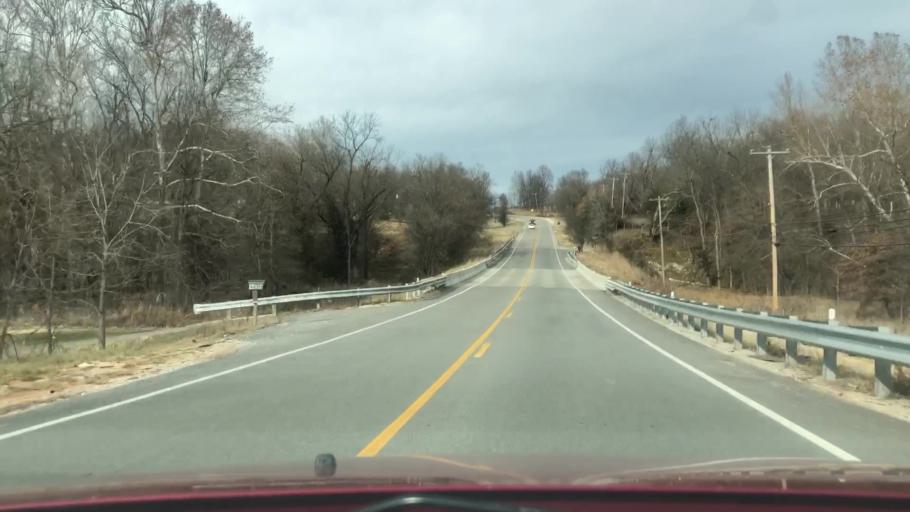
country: US
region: Missouri
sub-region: Greene County
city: Springfield
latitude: 37.2753
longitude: -93.2634
